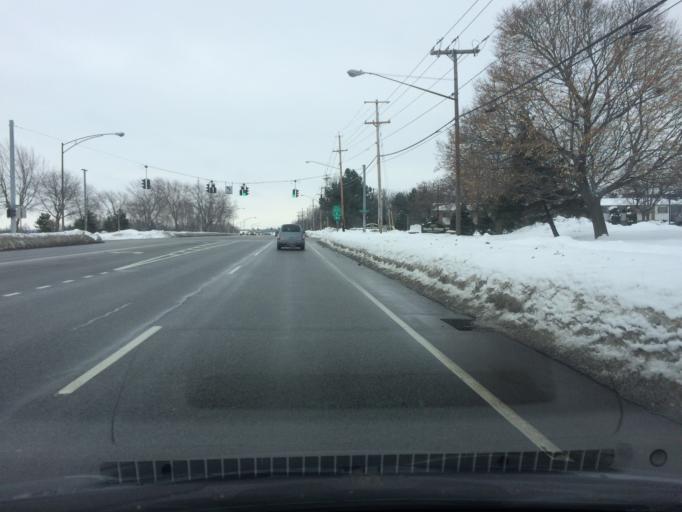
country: US
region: New York
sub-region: Monroe County
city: Rochester
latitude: 43.1013
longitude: -77.6147
